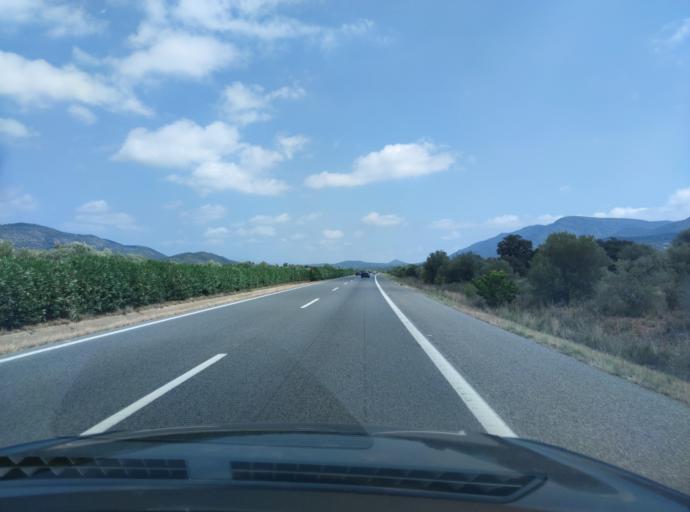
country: ES
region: Catalonia
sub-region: Provincia de Tarragona
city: Ulldecona
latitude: 40.6179
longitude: 0.4829
